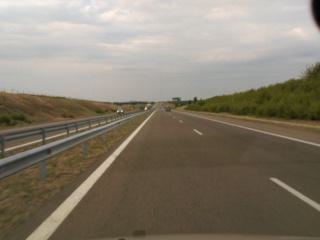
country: BG
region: Burgas
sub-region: Obshtina Karnobat
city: Karnobat
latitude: 42.5895
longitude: 27.0351
